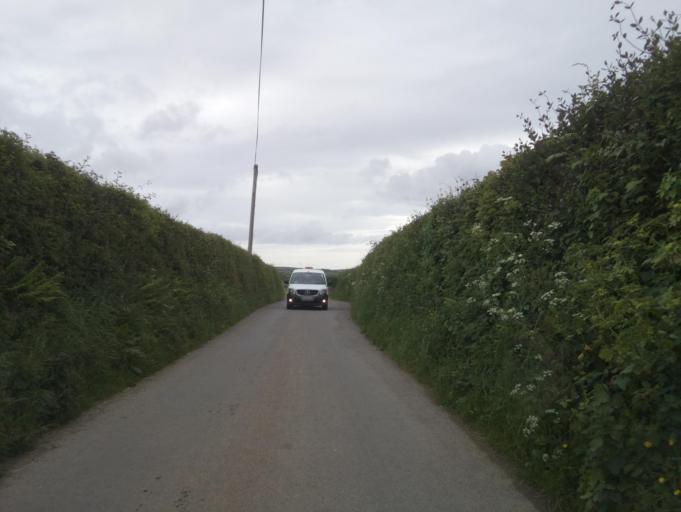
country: GB
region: England
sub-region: Devon
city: Dartmouth
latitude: 50.3196
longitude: -3.6293
